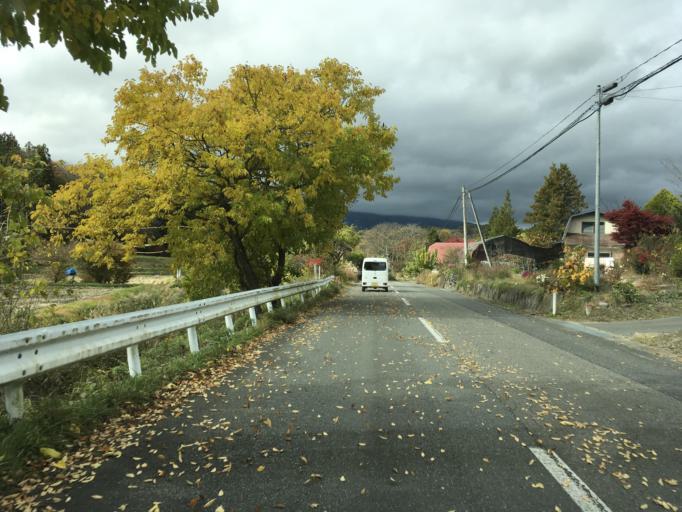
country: JP
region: Iwate
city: Mizusawa
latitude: 39.0625
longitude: 141.3889
